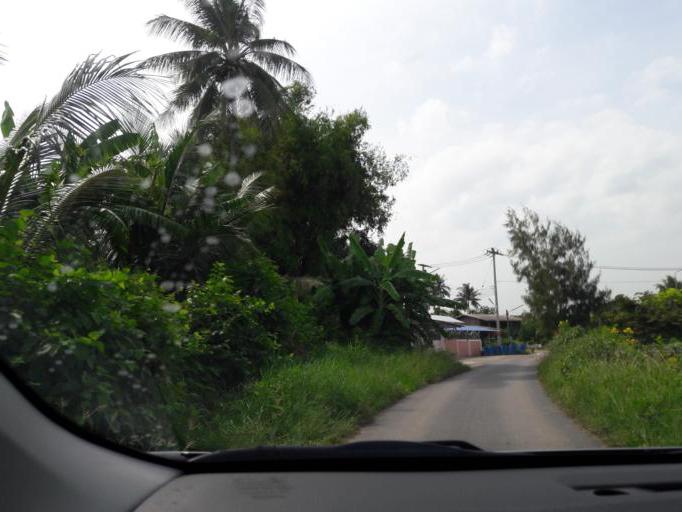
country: TH
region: Ang Thong
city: Ang Thong
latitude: 14.5765
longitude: 100.4750
